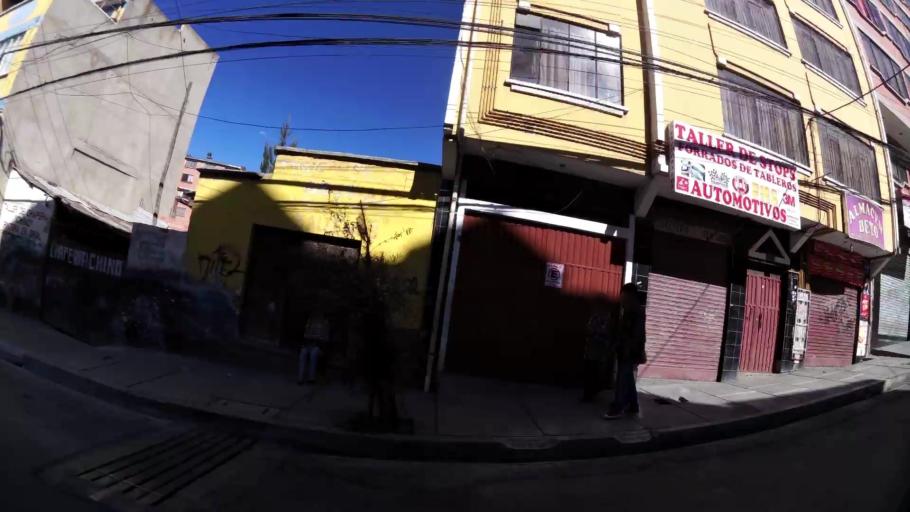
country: BO
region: La Paz
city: La Paz
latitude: -16.5107
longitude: -68.1378
